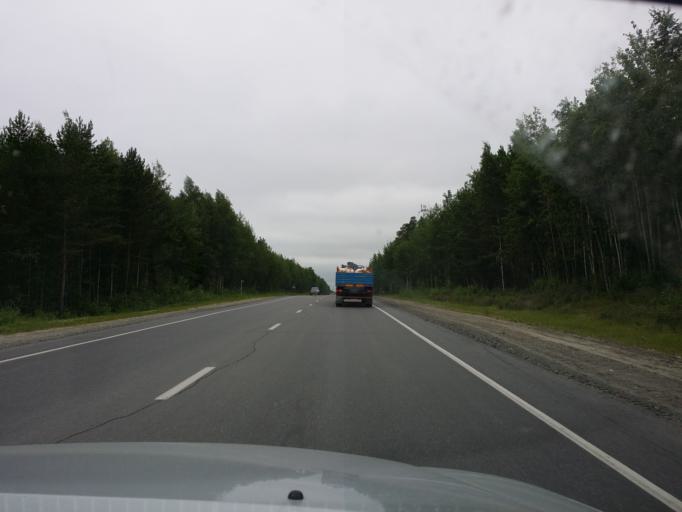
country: RU
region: Khanty-Mansiyskiy Avtonomnyy Okrug
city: Megion
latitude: 61.0551
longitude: 76.3068
